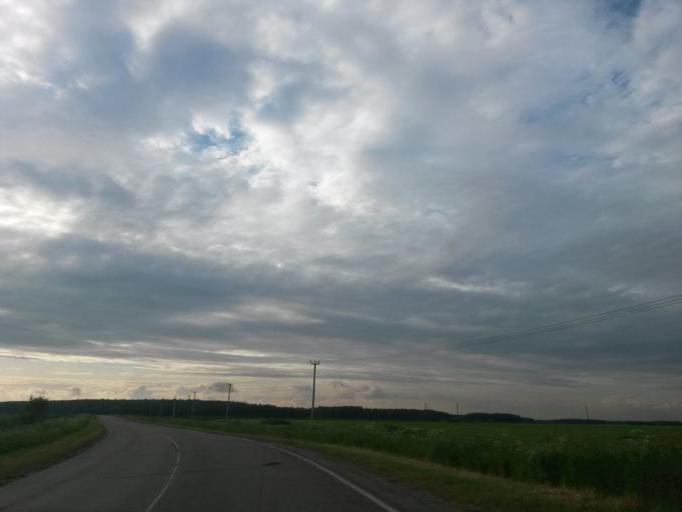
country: RU
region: Moskovskaya
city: Melikhovo
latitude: 55.1930
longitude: 37.7000
